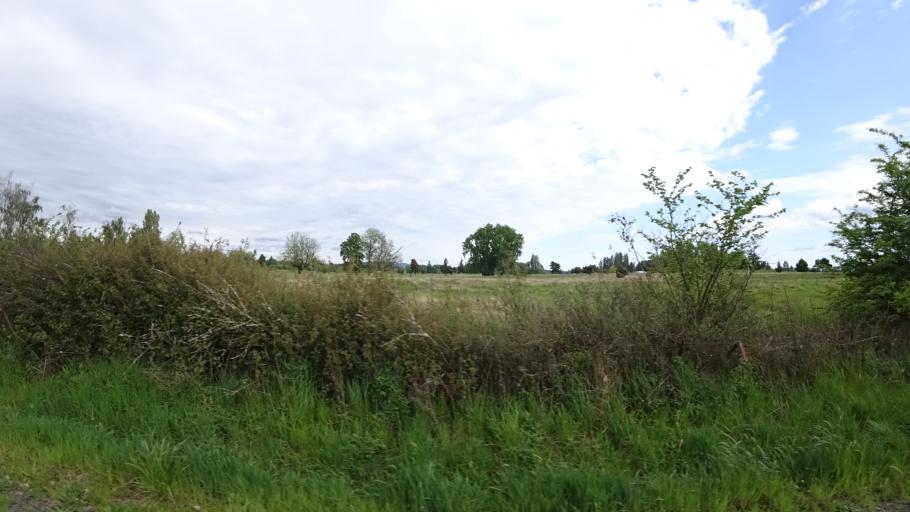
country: US
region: Oregon
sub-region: Washington County
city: Hillsboro
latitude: 45.4803
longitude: -122.9516
